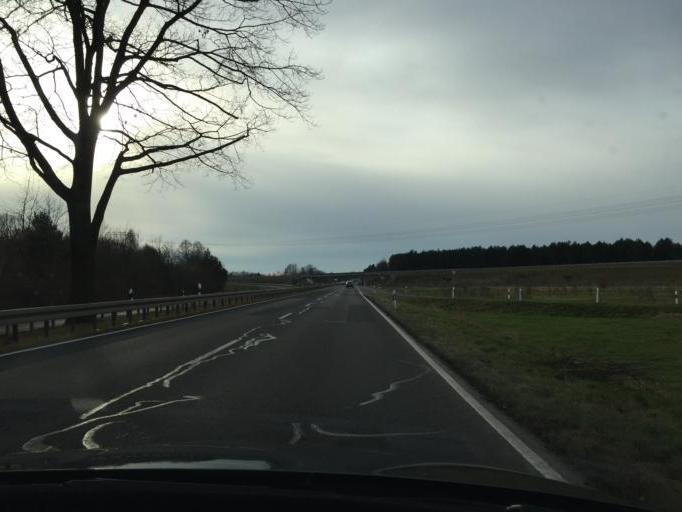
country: DE
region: Brandenburg
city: Cottbus
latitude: 51.7897
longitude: 14.3759
